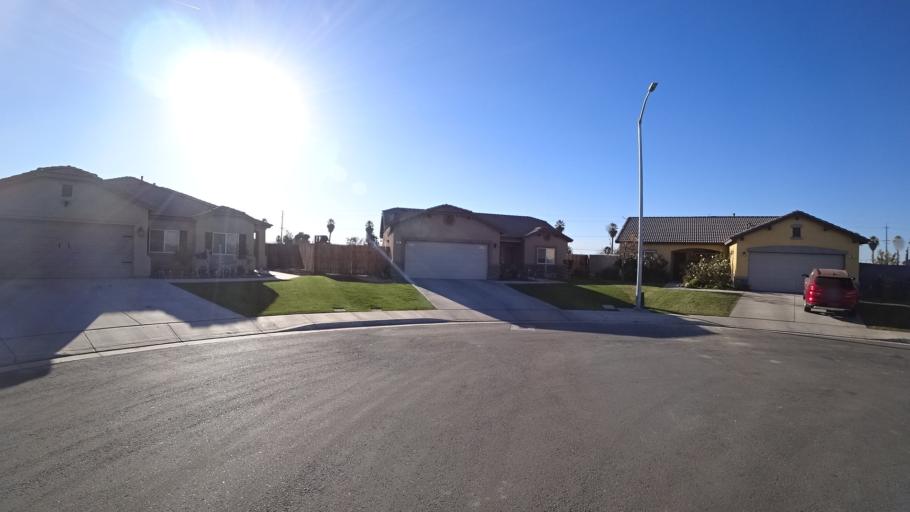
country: US
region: California
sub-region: Kern County
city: Greenfield
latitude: 35.2778
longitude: -119.0014
